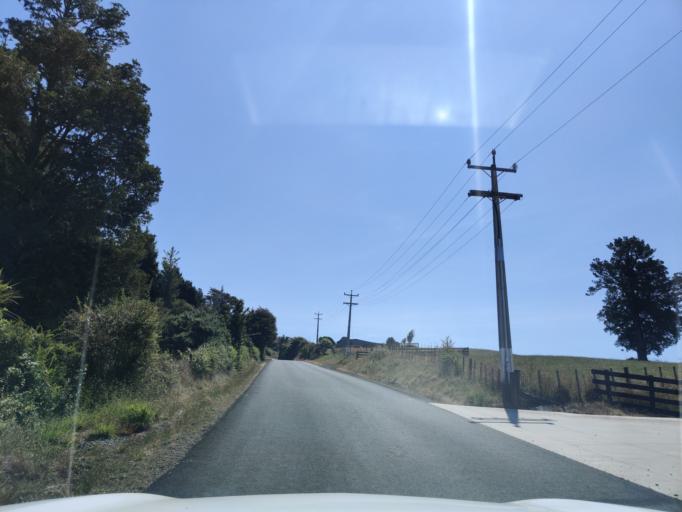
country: NZ
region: Auckland
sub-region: Auckland
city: Red Hill
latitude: -37.0630
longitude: 175.0821
